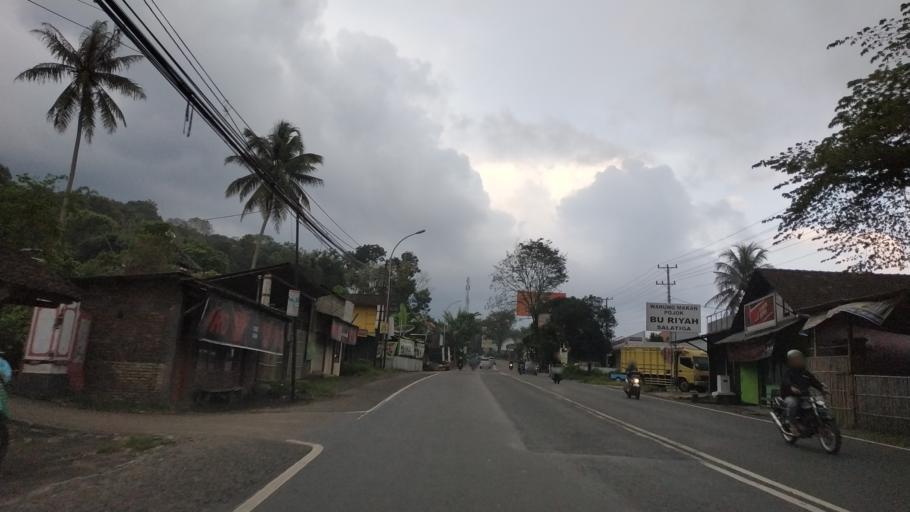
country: ID
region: Central Java
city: Salatiga
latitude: -7.2938
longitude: 110.4710
